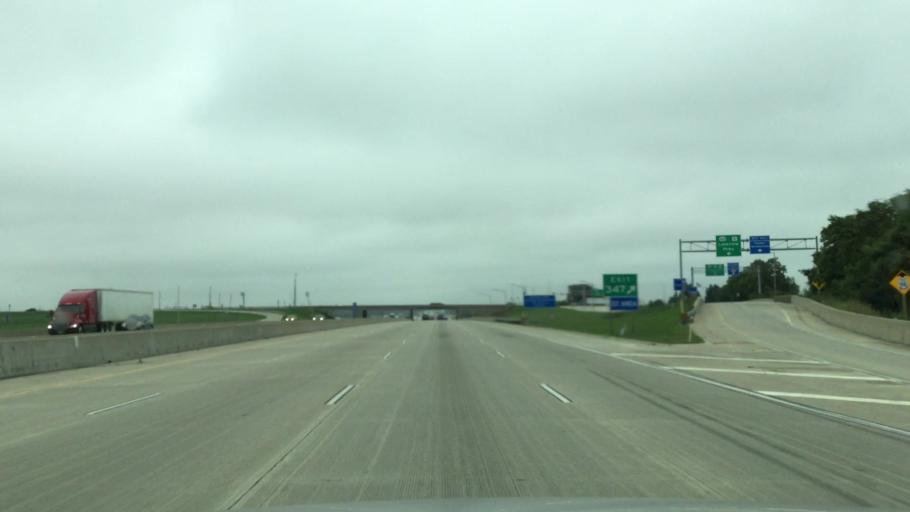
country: US
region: Wisconsin
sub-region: Kenosha County
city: Pleasant Prairie
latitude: 42.5196
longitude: -87.9516
